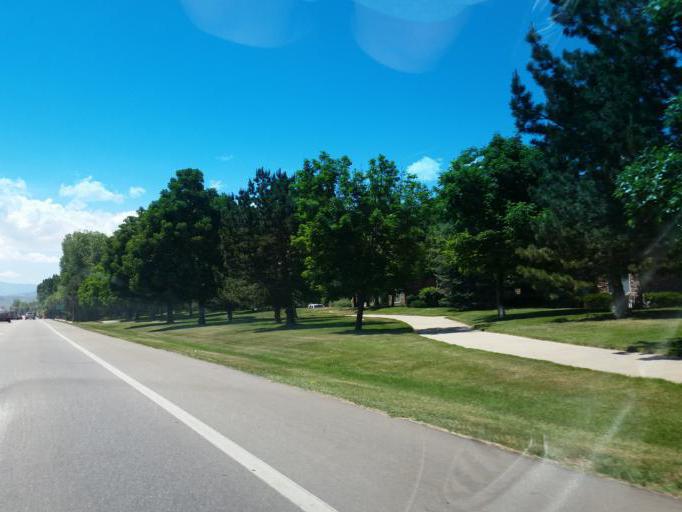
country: US
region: Colorado
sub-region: Larimer County
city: Fort Collins
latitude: 40.5238
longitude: -105.0537
